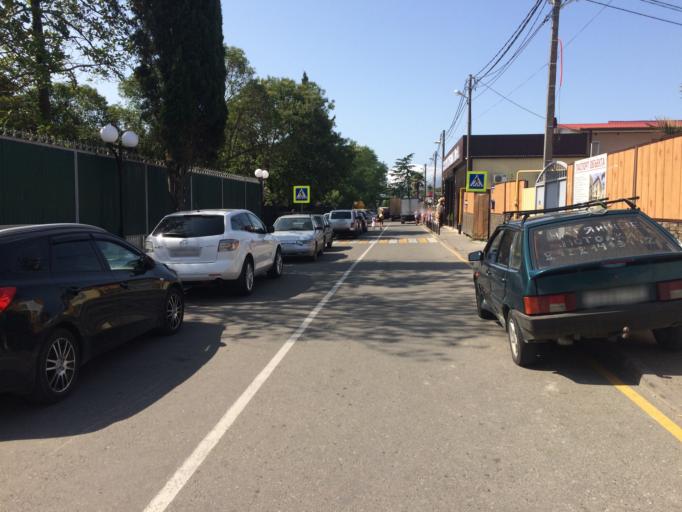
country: RU
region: Krasnodarskiy
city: Adler
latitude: 43.3981
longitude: 39.9668
